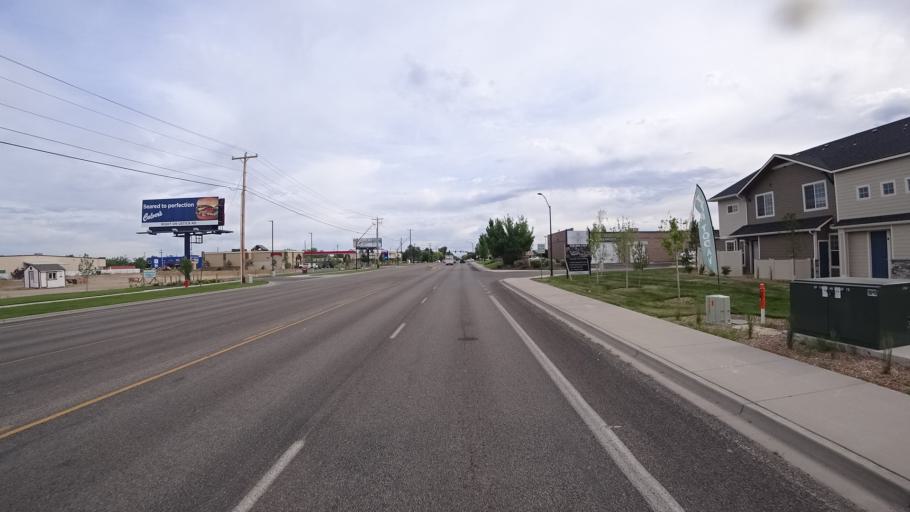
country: US
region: Idaho
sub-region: Ada County
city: Meridian
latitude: 43.6178
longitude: -116.3744
